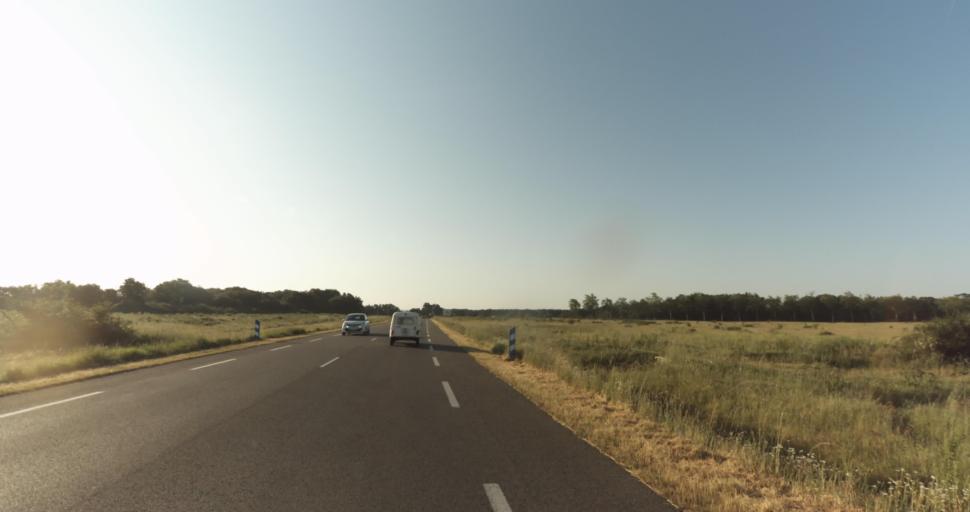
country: FR
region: Midi-Pyrenees
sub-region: Departement de la Haute-Garonne
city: Fontenilles
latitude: 43.5277
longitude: 1.2016
